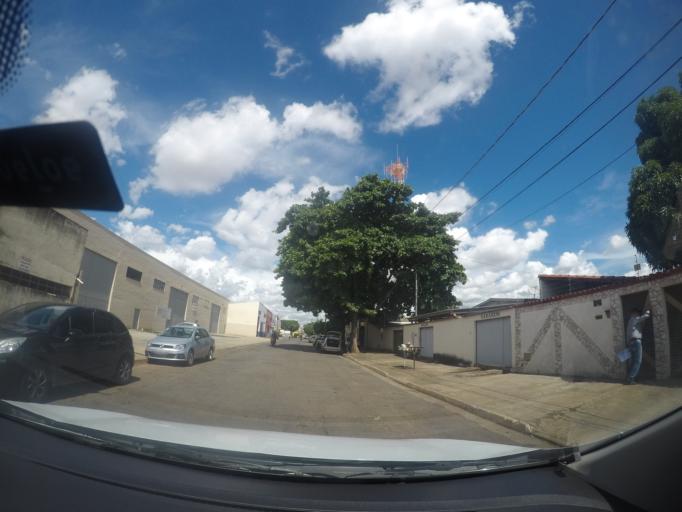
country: BR
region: Goias
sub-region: Goiania
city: Goiania
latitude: -16.6689
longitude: -49.3093
